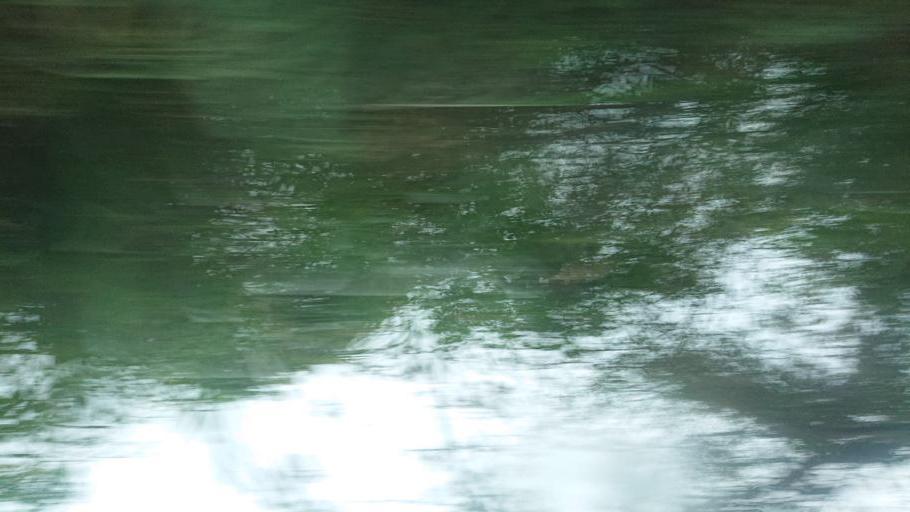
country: TW
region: Taiwan
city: Lugu
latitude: 23.5957
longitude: 120.7145
